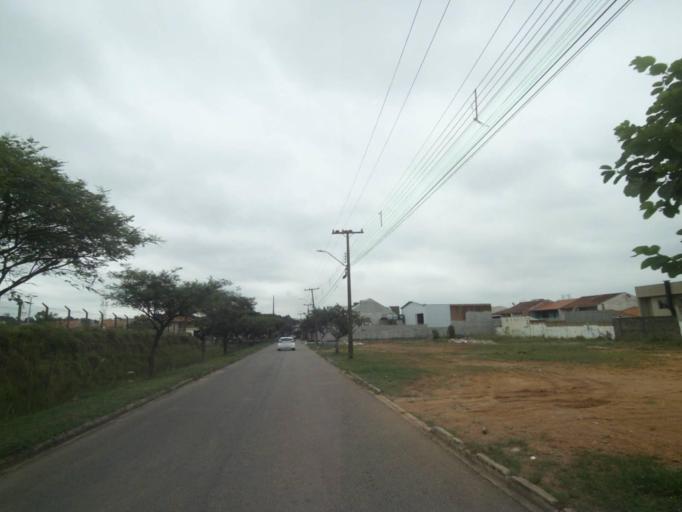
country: BR
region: Parana
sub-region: Araucaria
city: Araucaria
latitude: -25.5479
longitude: -49.3379
